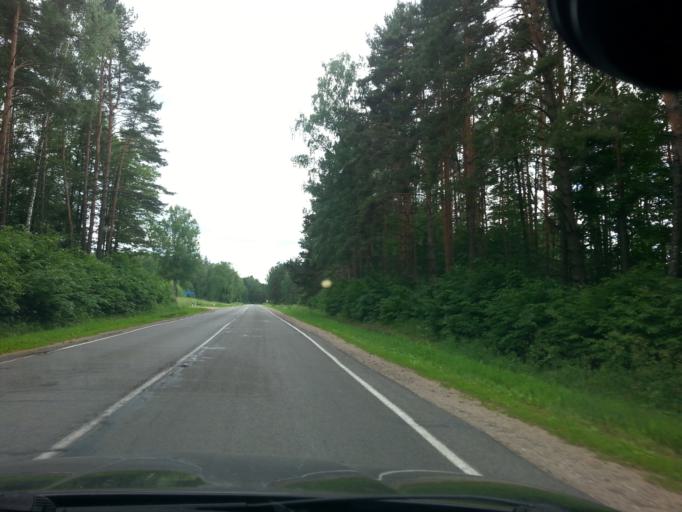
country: BY
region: Minsk
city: Svir
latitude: 54.8288
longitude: 26.1886
